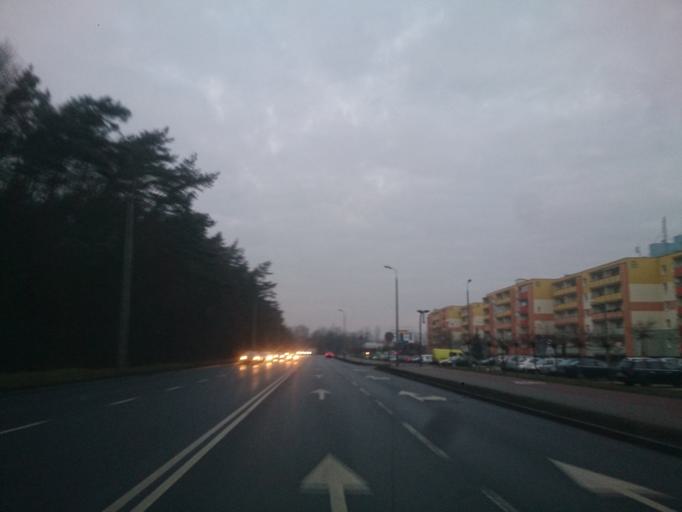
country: PL
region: Kujawsko-Pomorskie
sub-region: Grudziadz
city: Grudziadz
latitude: 53.4624
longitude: 18.7686
